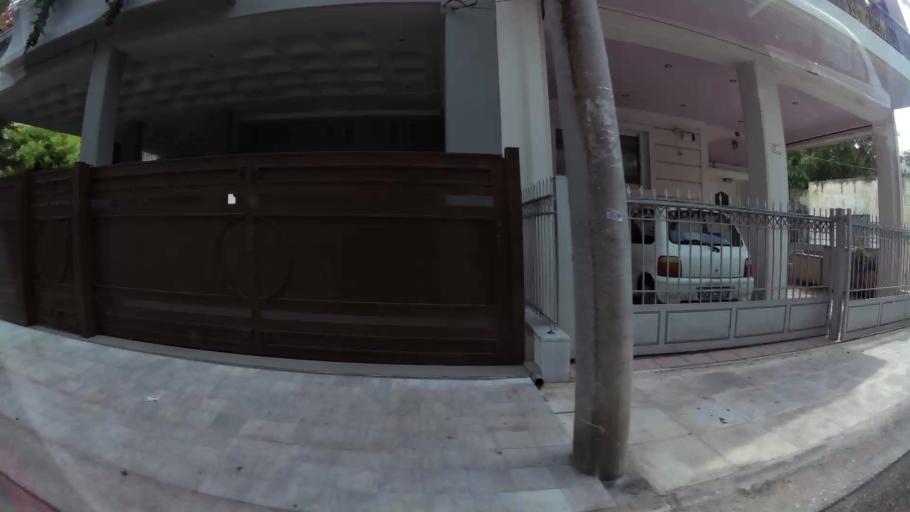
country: GR
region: Attica
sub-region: Nomarchia Athinas
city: Chaidari
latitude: 38.0253
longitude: 23.6755
